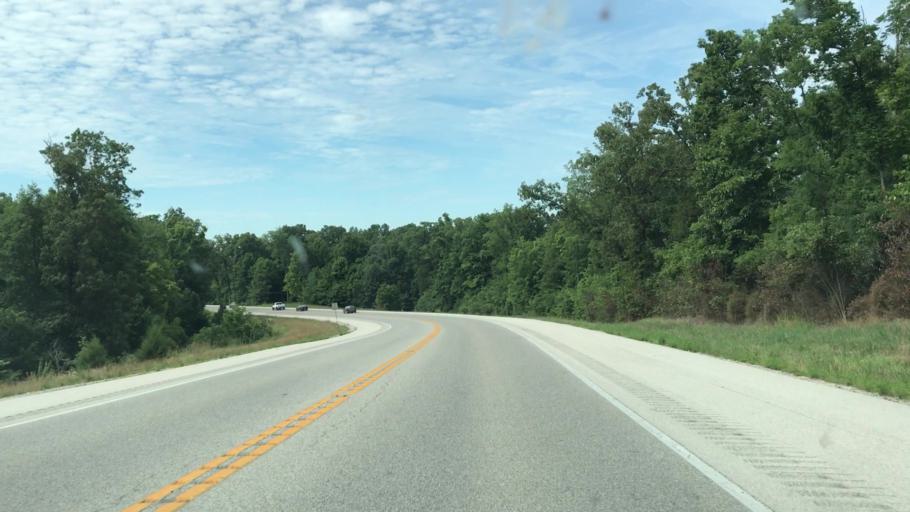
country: US
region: Kentucky
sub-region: Edmonson County
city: Brownsville
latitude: 37.0958
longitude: -86.2329
